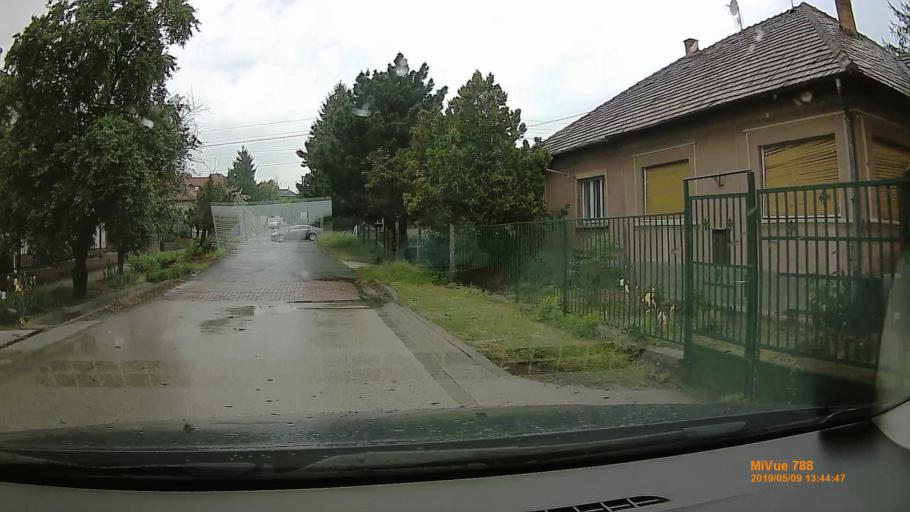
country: HU
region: Budapest
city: Budapest XVI. keruelet
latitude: 47.5326
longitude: 19.1919
